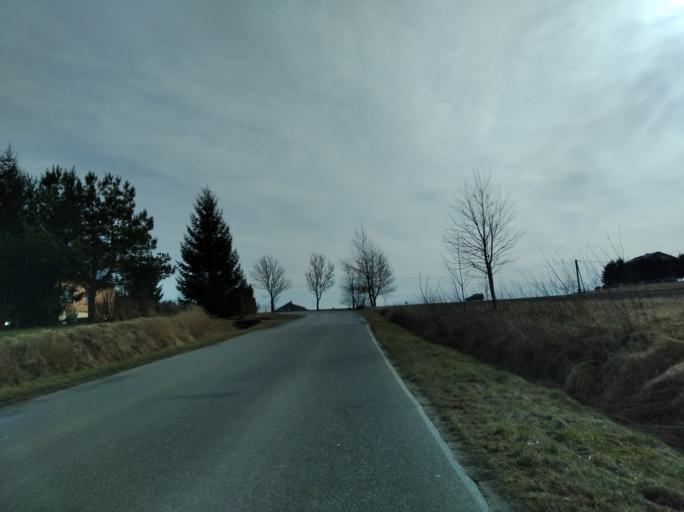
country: PL
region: Subcarpathian Voivodeship
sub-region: Powiat brzozowski
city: Orzechowka
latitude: 49.7199
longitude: 21.9639
